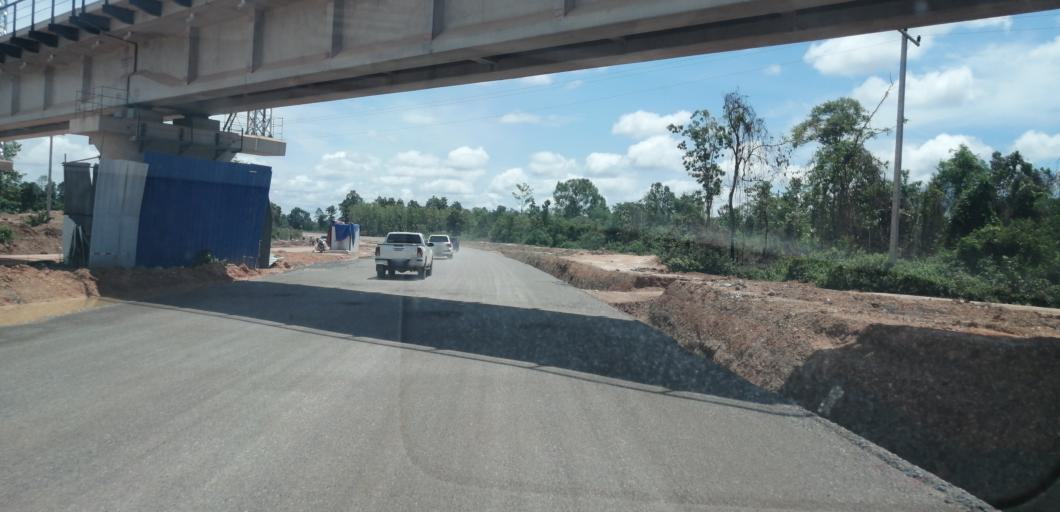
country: TH
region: Nong Khai
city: Sangkhom
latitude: 18.2268
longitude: 102.4820
